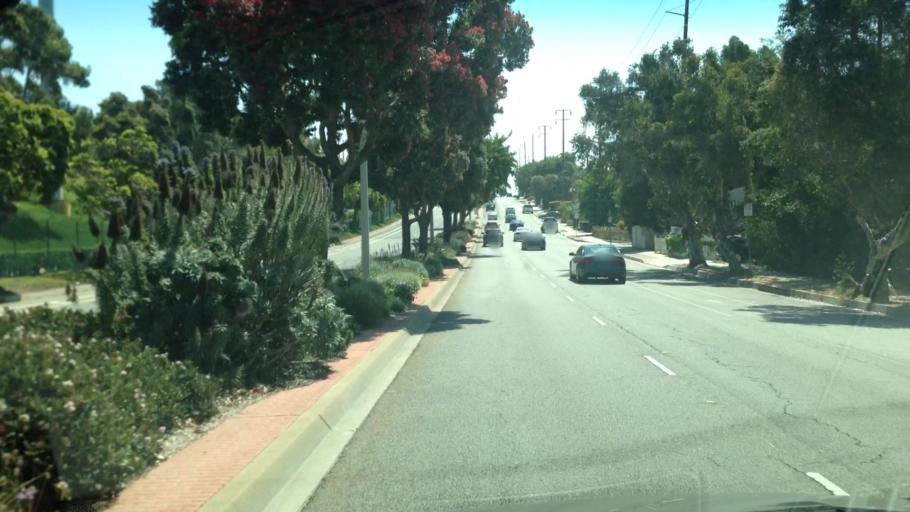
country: US
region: California
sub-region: Los Angeles County
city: Manhattan Beach
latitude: 33.9020
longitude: -118.4027
